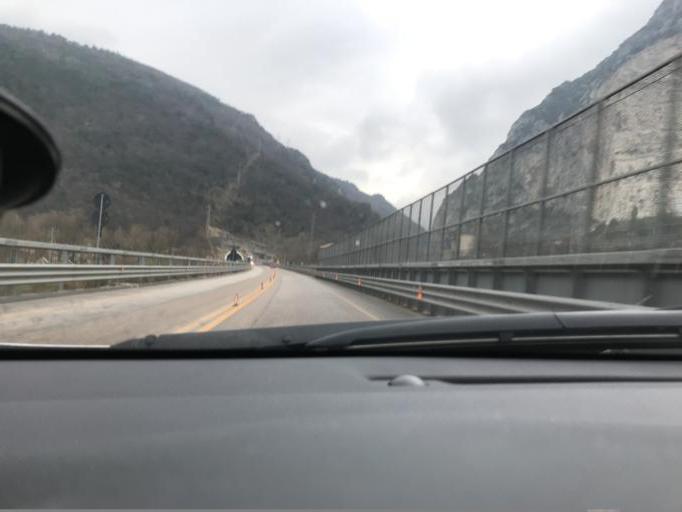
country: IT
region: The Marches
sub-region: Provincia di Ancona
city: Serra San Quirico
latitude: 43.4325
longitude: 13.0145
